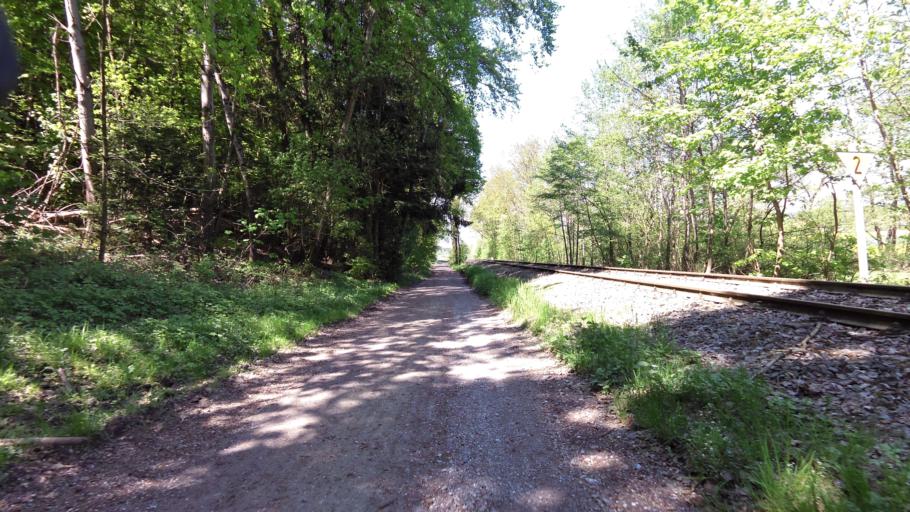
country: DE
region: Bavaria
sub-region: Lower Bavaria
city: Weihmichl
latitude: 48.5679
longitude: 12.0791
